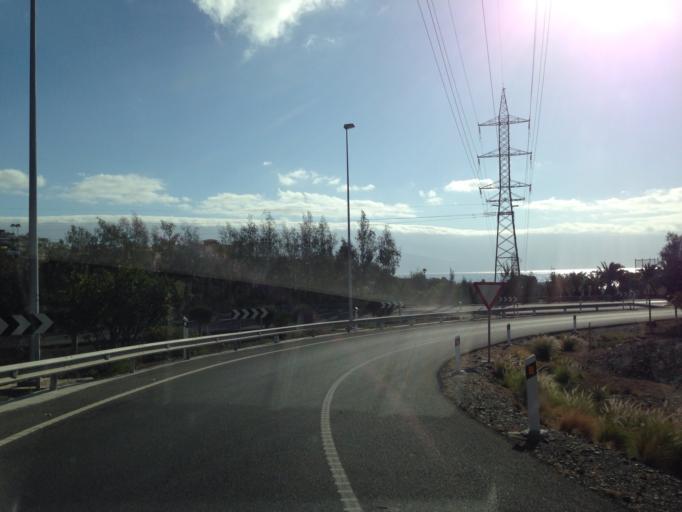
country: ES
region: Canary Islands
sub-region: Provincia de Las Palmas
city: Playa del Ingles
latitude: 27.7695
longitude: -15.5565
